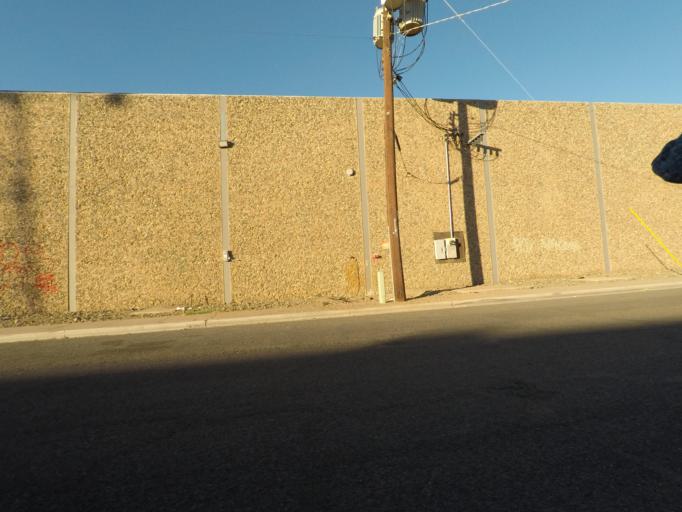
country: US
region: Arizona
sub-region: Maricopa County
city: Phoenix
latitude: 33.4683
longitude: -112.1079
